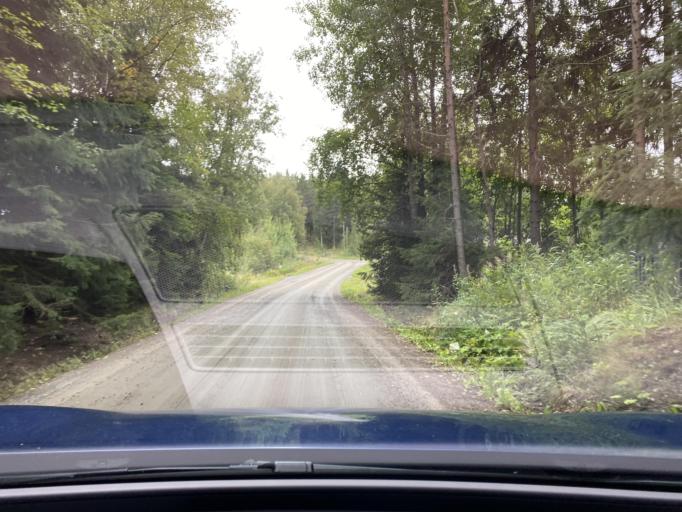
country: FI
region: Pirkanmaa
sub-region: Lounais-Pirkanmaa
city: Vammala
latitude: 61.2606
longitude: 23.0125
